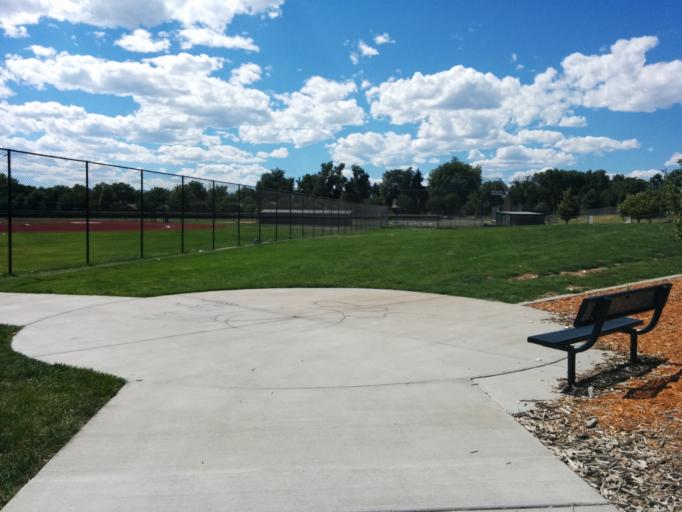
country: US
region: Colorado
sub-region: Arapahoe County
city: Glendale
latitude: 39.6907
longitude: -104.9662
